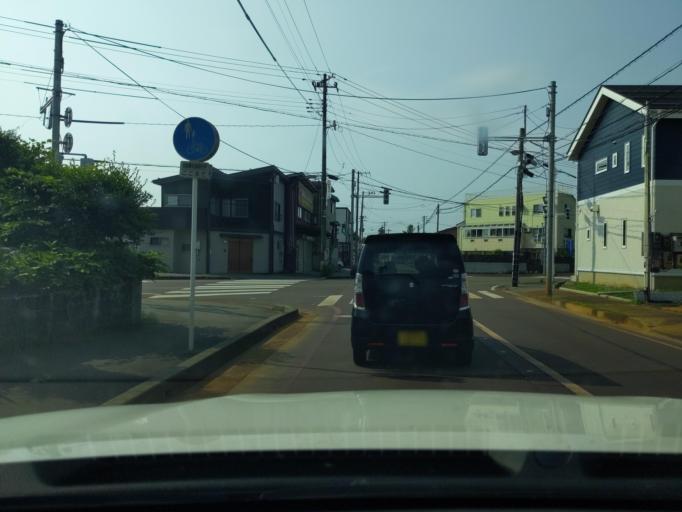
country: JP
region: Niigata
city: Nagaoka
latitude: 37.4335
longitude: 138.8586
